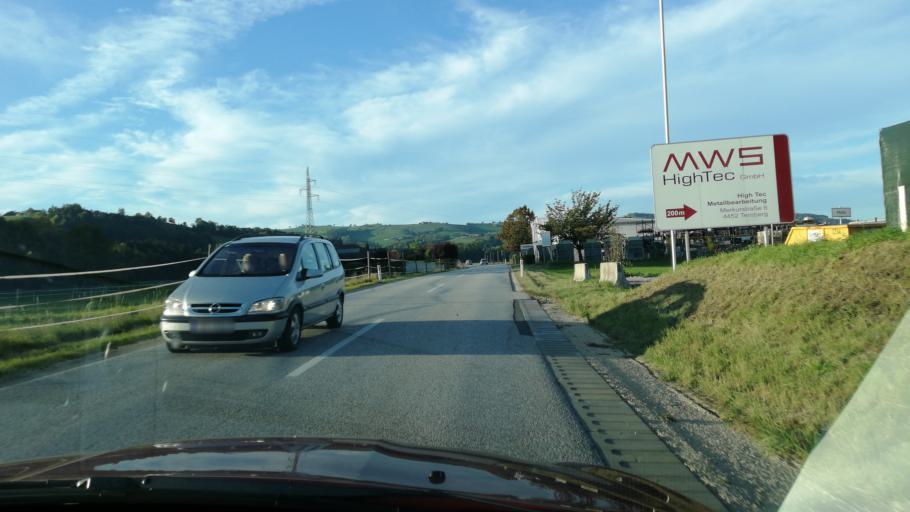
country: AT
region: Upper Austria
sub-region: Politischer Bezirk Steyr-Land
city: Ternberg
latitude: 47.9555
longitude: 14.3525
